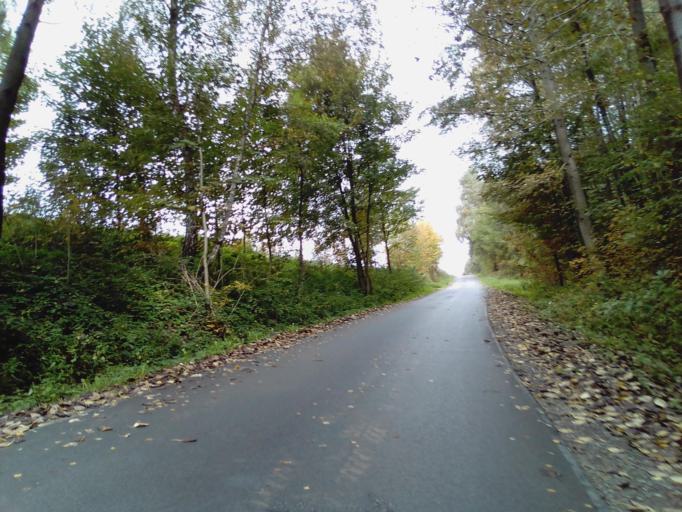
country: PL
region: Subcarpathian Voivodeship
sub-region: Powiat strzyzowski
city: Gwoznica Gorna
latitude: 49.8343
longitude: 22.0052
